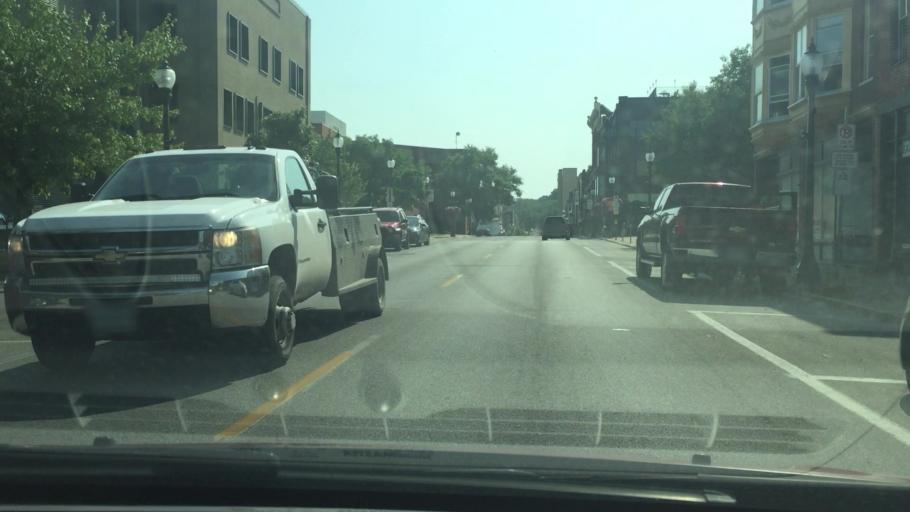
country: US
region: Iowa
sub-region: Muscatine County
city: Muscatine
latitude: 41.4235
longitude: -91.0417
